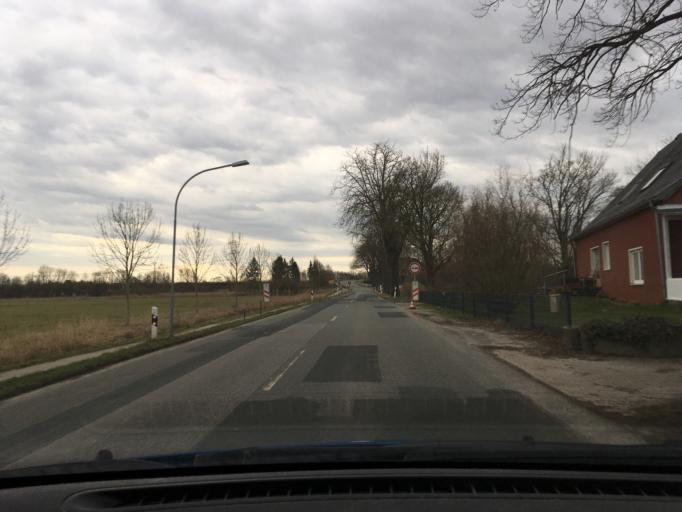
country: DE
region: Lower Saxony
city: Handorf
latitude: 53.3609
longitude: 10.3391
